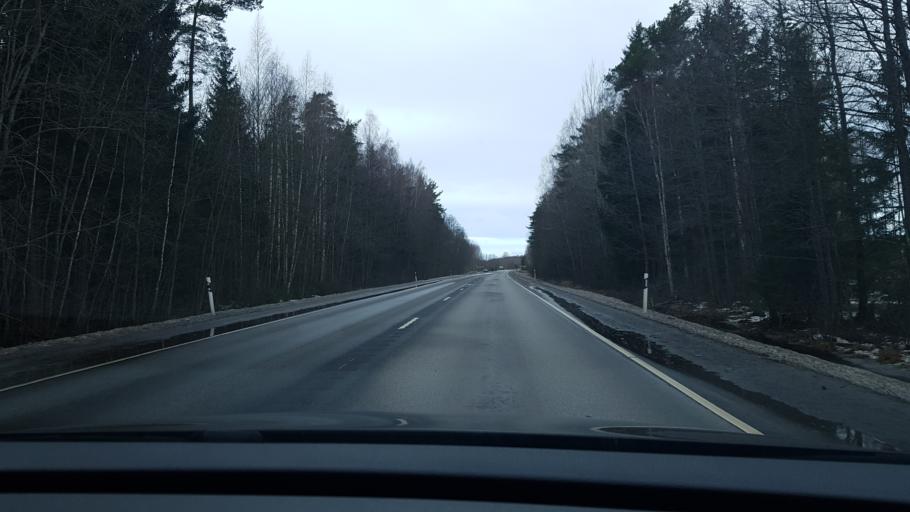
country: EE
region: Paernumaa
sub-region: Paikuse vald
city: Paikuse
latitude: 58.2842
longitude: 24.6092
